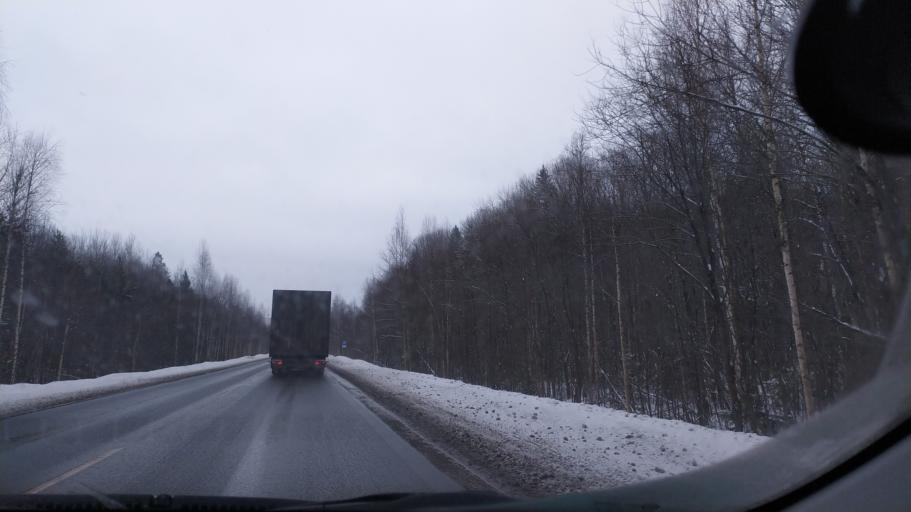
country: RU
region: Chuvashia
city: Mariinskiy Posad
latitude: 56.1815
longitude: 47.8637
